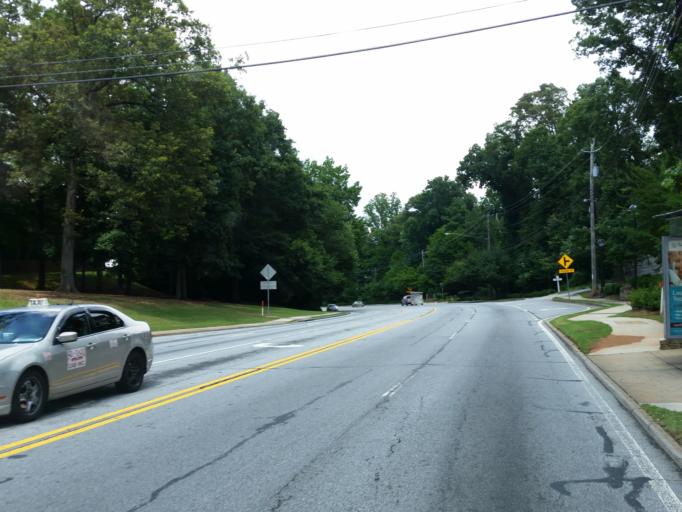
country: US
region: Georgia
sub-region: DeKalb County
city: Dunwoody
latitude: 33.9750
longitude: -84.3537
